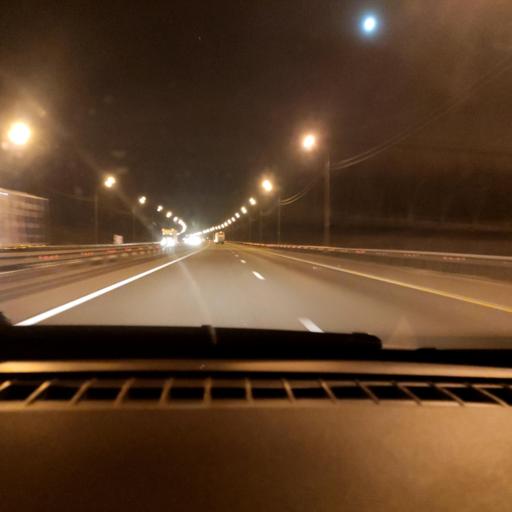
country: RU
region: Lipetsk
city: Khlevnoye
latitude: 52.2232
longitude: 39.1111
